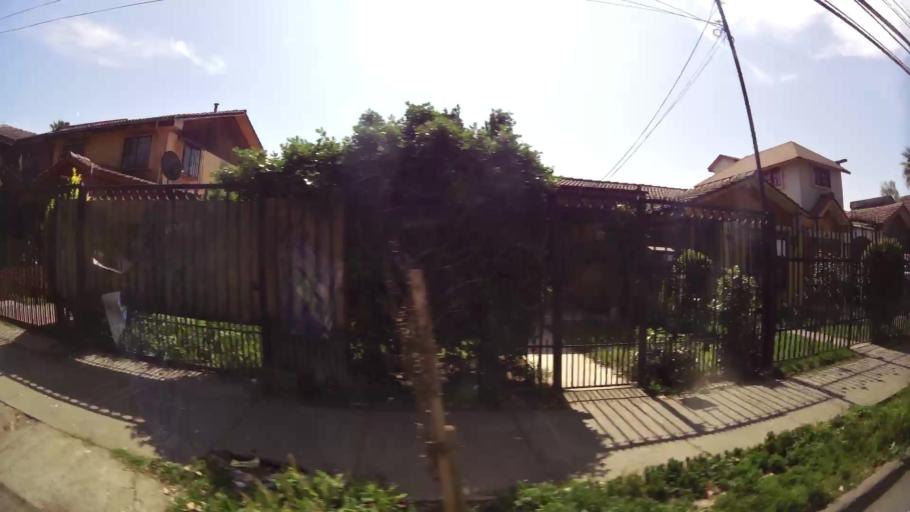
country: CL
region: Santiago Metropolitan
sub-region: Provincia de Santiago
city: Lo Prado
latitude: -33.4691
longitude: -70.7343
